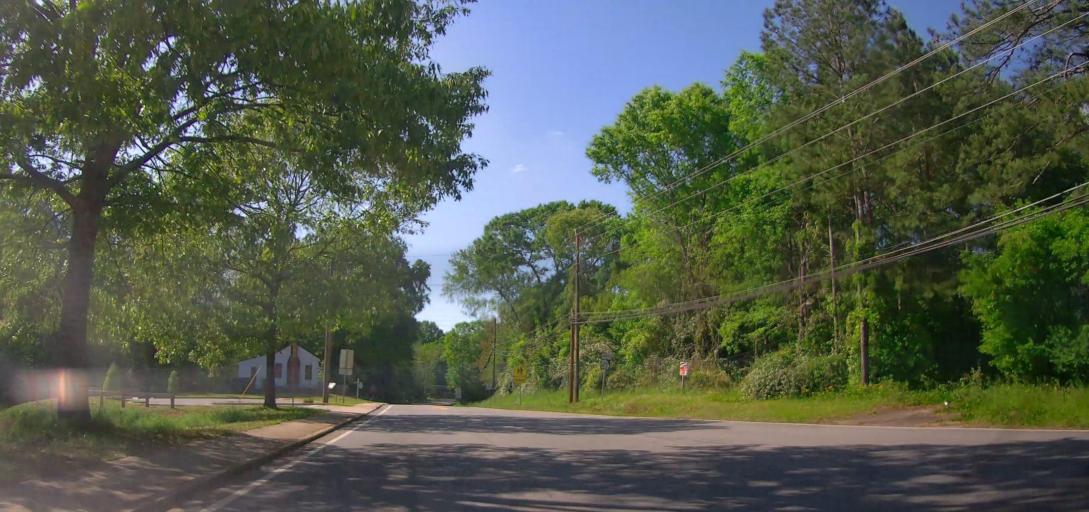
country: US
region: Georgia
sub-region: Morgan County
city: Madison
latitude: 33.5995
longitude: -83.4725
